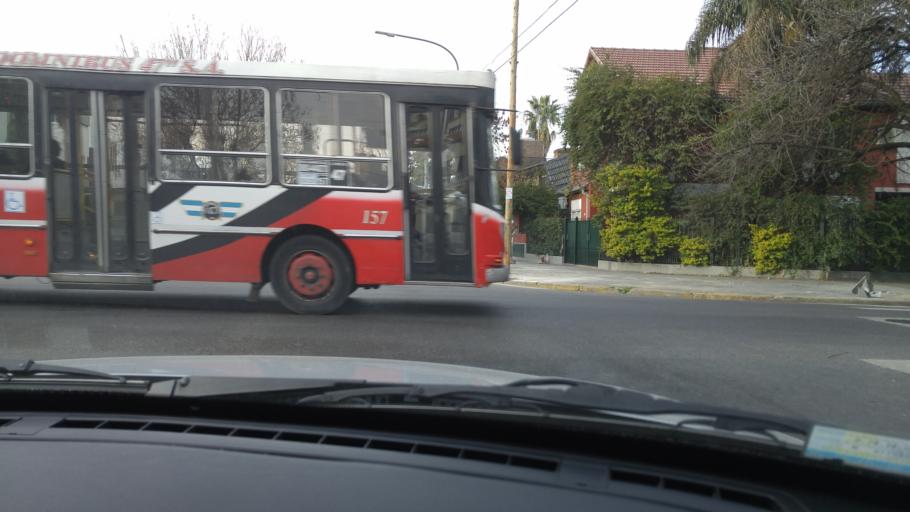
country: AR
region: Buenos Aires F.D.
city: Villa Santa Rita
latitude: -34.6285
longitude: -58.5176
